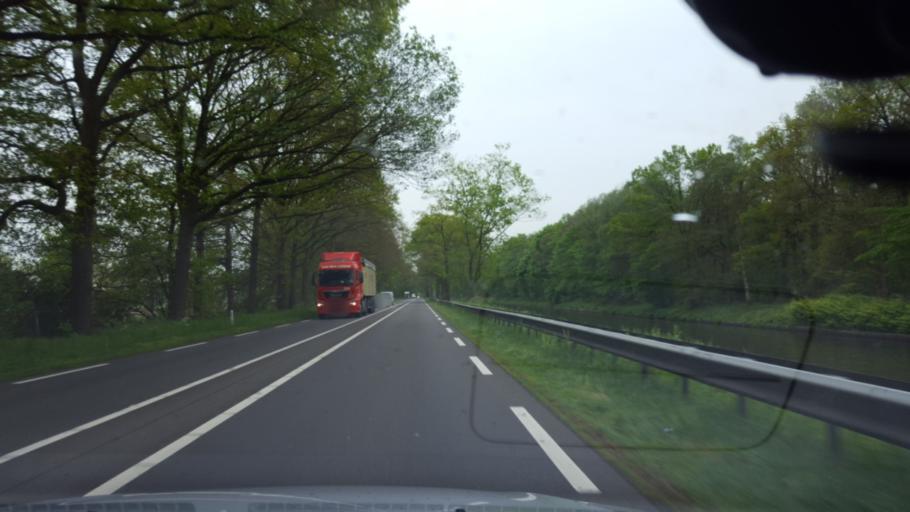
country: NL
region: North Brabant
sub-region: Gemeente Veghel
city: Keldonk
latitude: 51.5628
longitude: 5.6040
